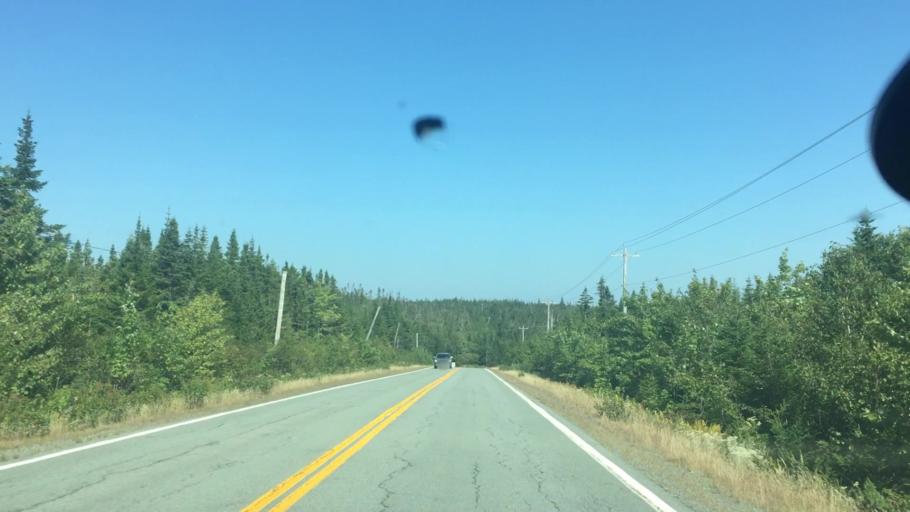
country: CA
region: Nova Scotia
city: Antigonish
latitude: 45.0108
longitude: -62.1054
